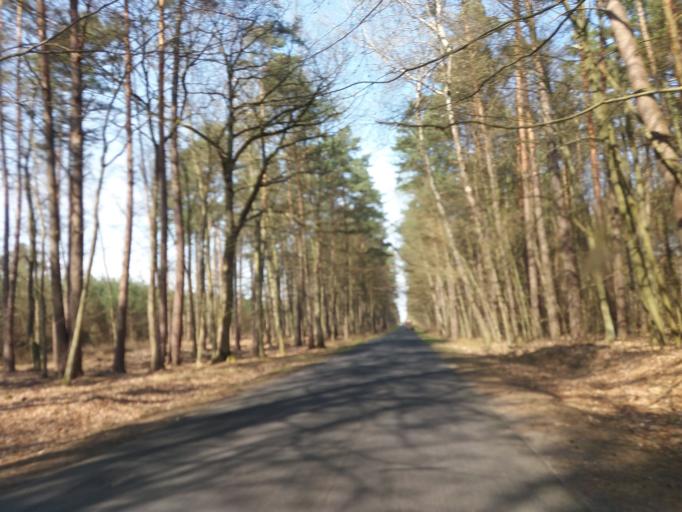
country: PL
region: West Pomeranian Voivodeship
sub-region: Powiat choszczenski
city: Recz
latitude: 53.2025
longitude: 15.6302
